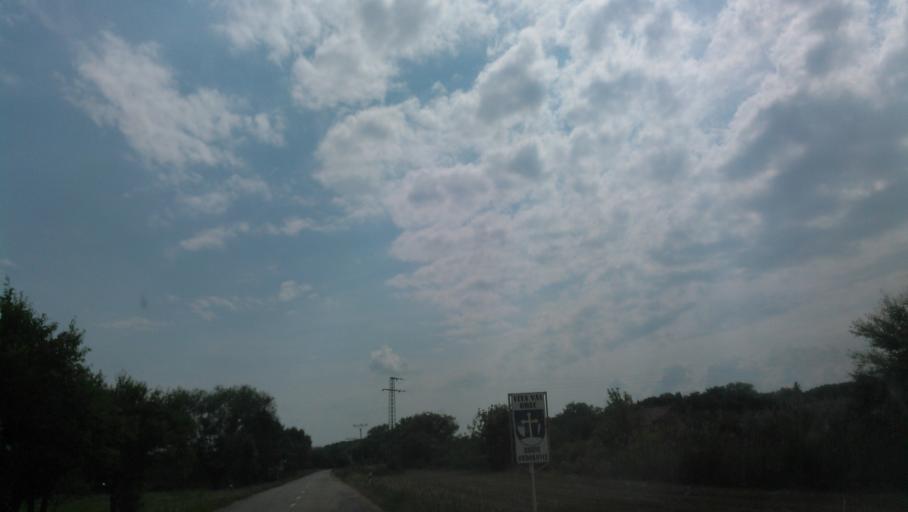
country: SK
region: Nitriansky
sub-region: Okres Nitra
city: Nitra
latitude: 48.4989
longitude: 18.0555
